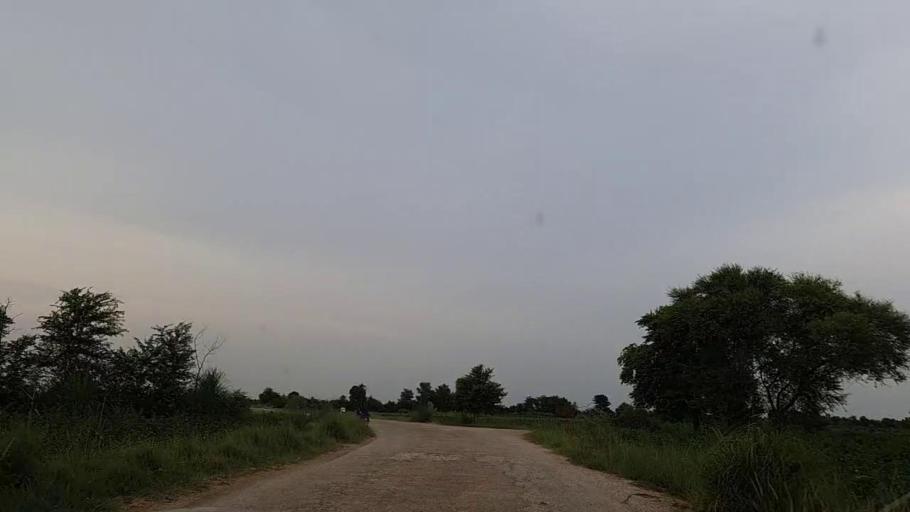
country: PK
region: Sindh
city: Mirpur Mathelo
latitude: 27.8754
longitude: 69.6363
